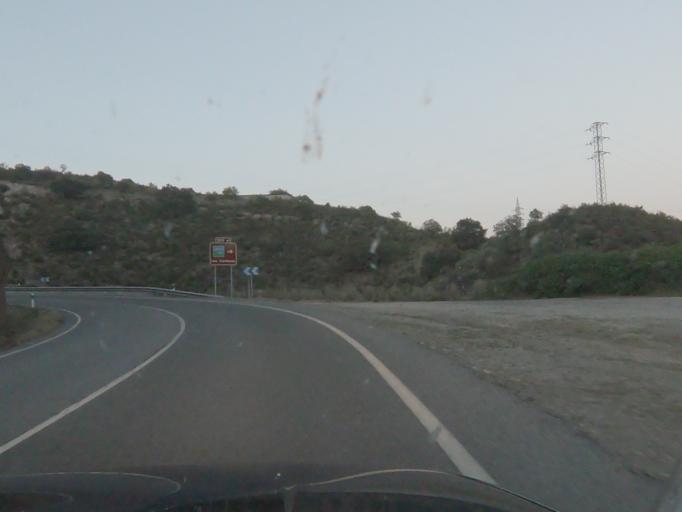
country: ES
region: Extremadura
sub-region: Provincia de Caceres
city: Alcantara
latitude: 39.7262
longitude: -6.8926
